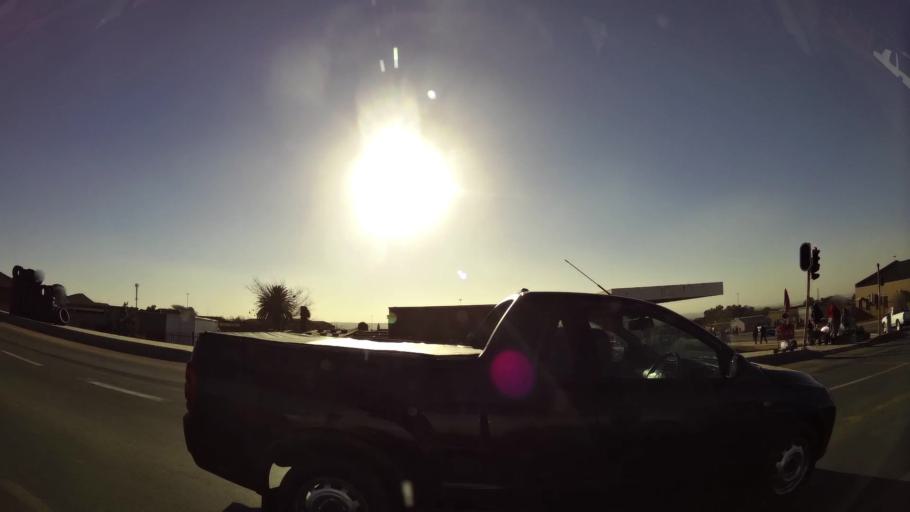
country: ZA
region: Gauteng
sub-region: Ekurhuleni Metropolitan Municipality
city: Tembisa
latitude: -26.0013
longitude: 28.2225
